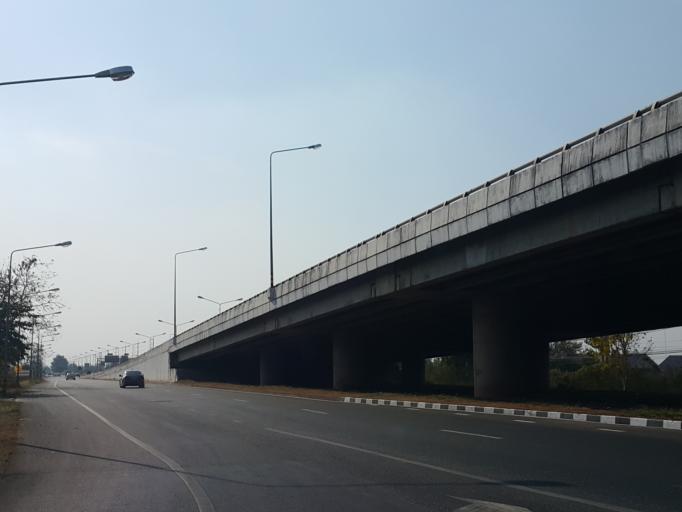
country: TH
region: Phitsanulok
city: Wang Thong
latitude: 16.8471
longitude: 100.3443
